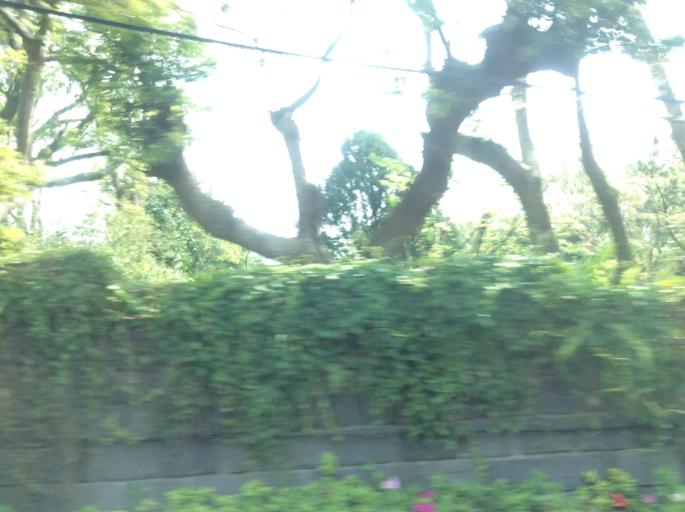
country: TW
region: Taipei
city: Taipei
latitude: 25.1208
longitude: 121.5529
